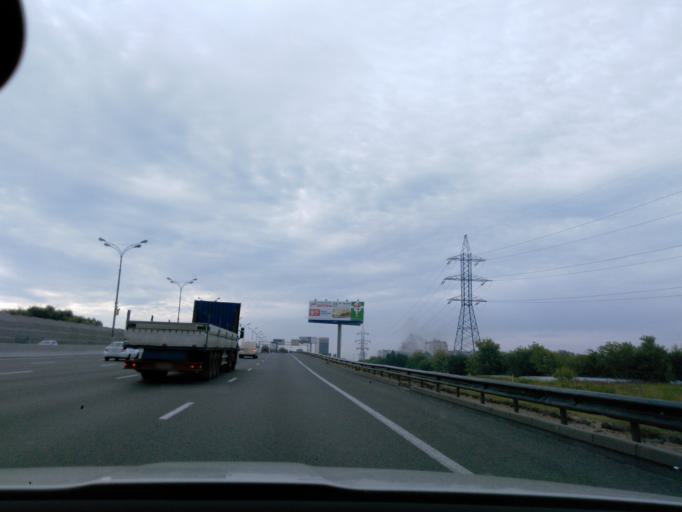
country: RU
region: Moscow
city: Yaroslavskiy
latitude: 55.8884
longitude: 37.7135
